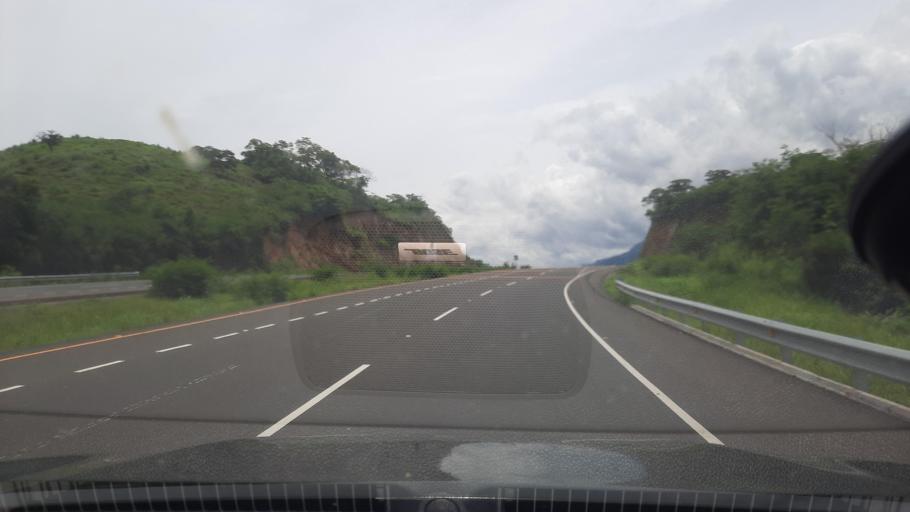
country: HN
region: Valle
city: Aramecina
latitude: 13.7453
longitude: -87.7177
